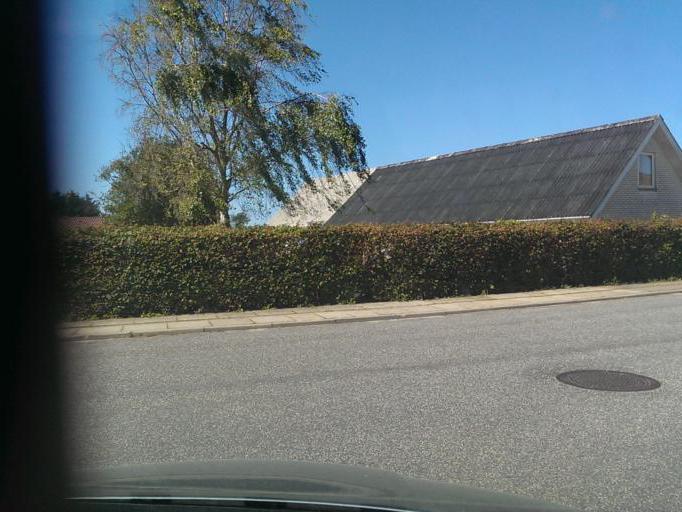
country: DK
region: North Denmark
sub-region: Jammerbugt Kommune
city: Pandrup
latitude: 57.3156
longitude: 9.7107
